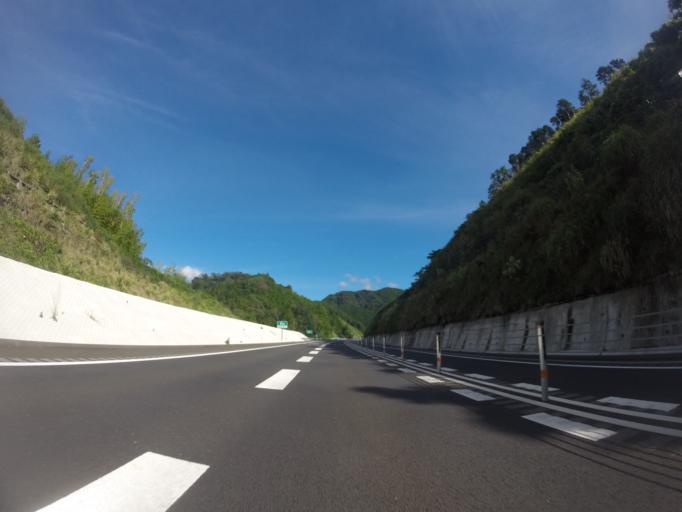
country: JP
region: Shizuoka
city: Shizuoka-shi
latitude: 35.1232
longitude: 138.4528
